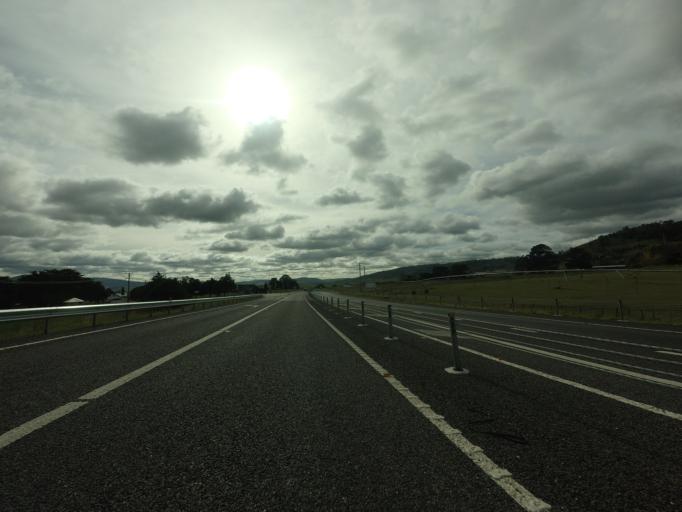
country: AU
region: Tasmania
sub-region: Brighton
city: Bridgewater
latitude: -42.5420
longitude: 147.2062
